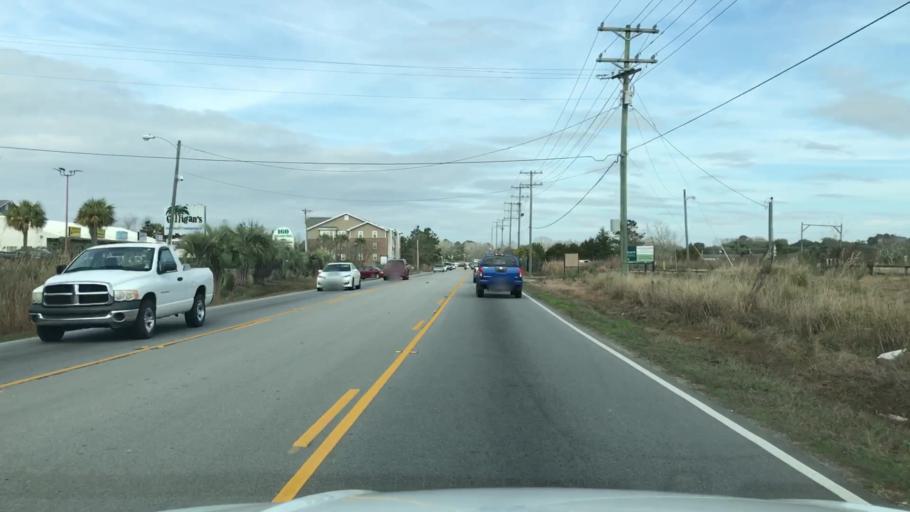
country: US
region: South Carolina
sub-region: Charleston County
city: Shell Point
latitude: 32.7979
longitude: -80.1086
